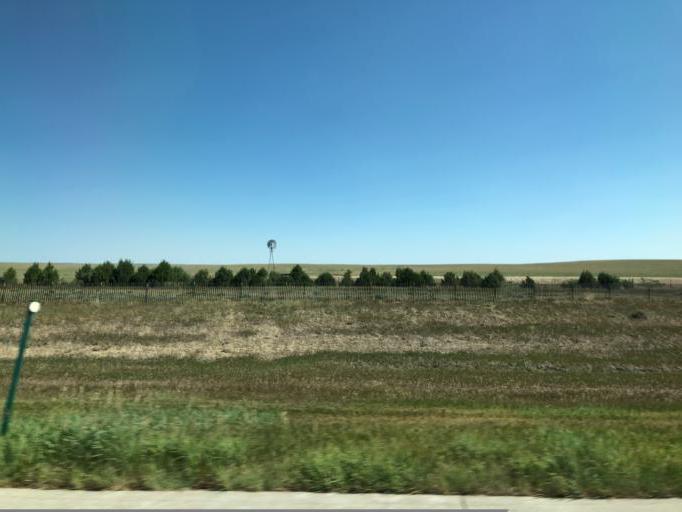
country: US
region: Colorado
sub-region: Lincoln County
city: Limon
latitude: 39.2751
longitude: -103.7425
